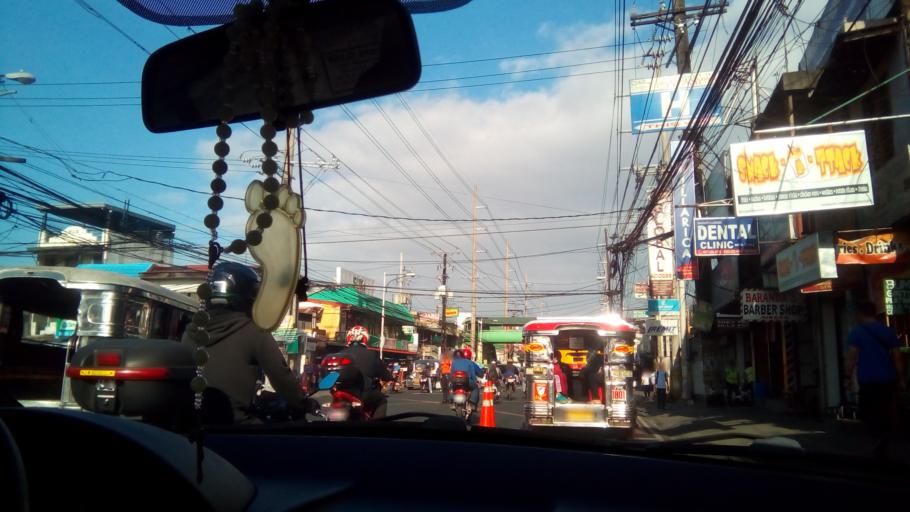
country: PH
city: Sambayanihan People's Village
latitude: 14.4367
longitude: 121.0071
